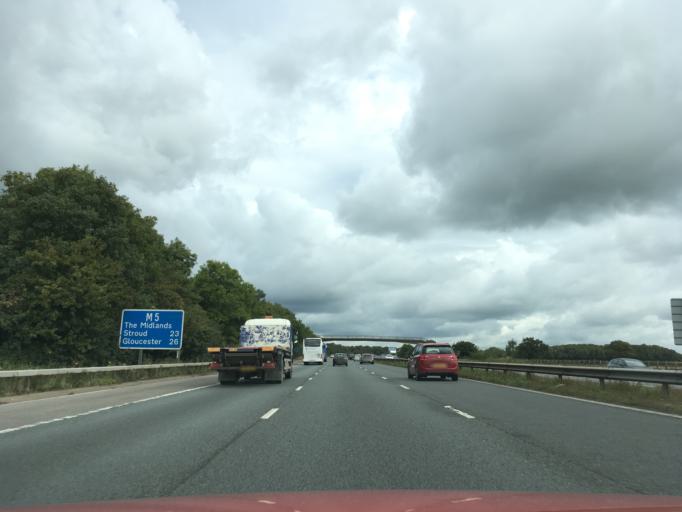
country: GB
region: England
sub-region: South Gloucestershire
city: Alveston
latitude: 51.5646
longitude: -2.5319
